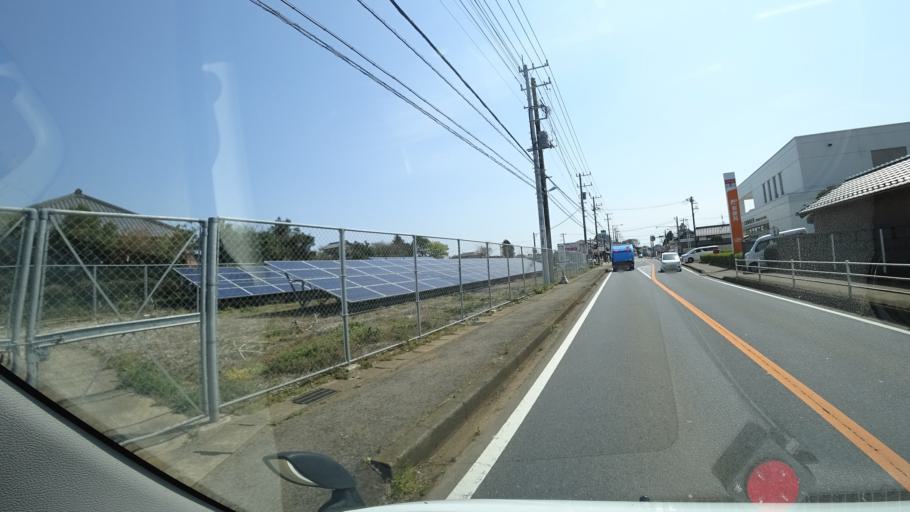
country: JP
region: Chiba
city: Narita
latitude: 35.7648
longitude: 140.3598
